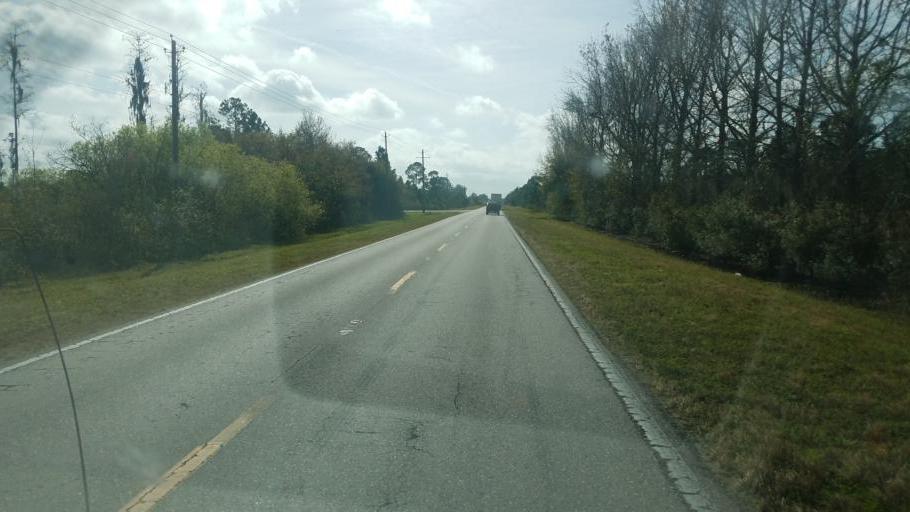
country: US
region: Florida
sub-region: Polk County
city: Polk City
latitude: 28.1949
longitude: -81.7505
